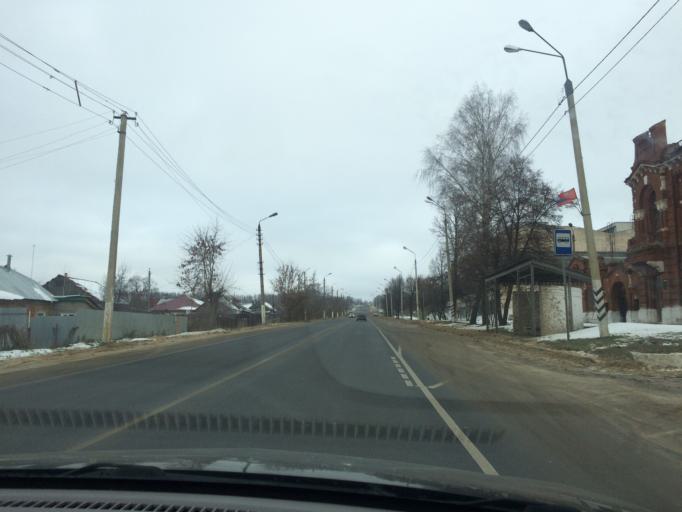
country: RU
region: Tula
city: Plavsk
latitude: 53.7133
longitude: 37.2964
